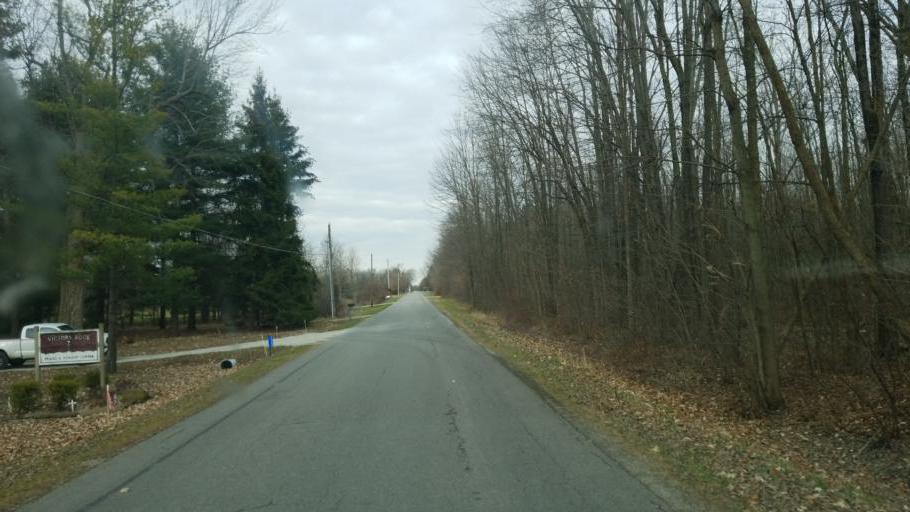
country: US
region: Ohio
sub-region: Crawford County
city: Galion
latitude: 40.7667
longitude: -82.7829
